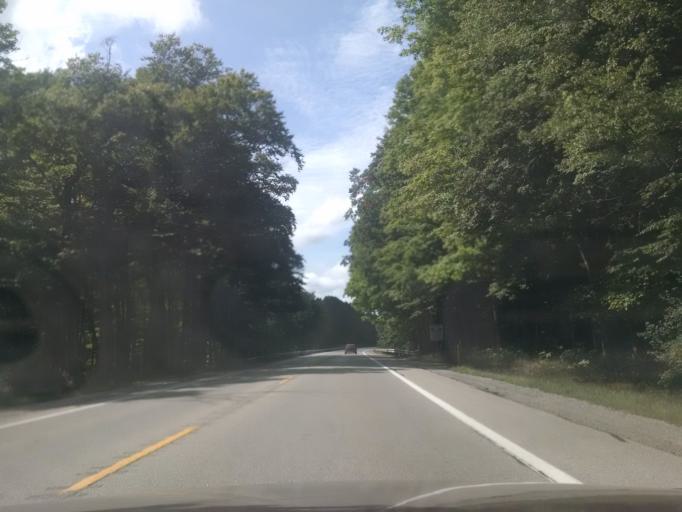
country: US
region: Michigan
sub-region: Clare County
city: Clare
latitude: 43.8707
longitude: -84.9318
